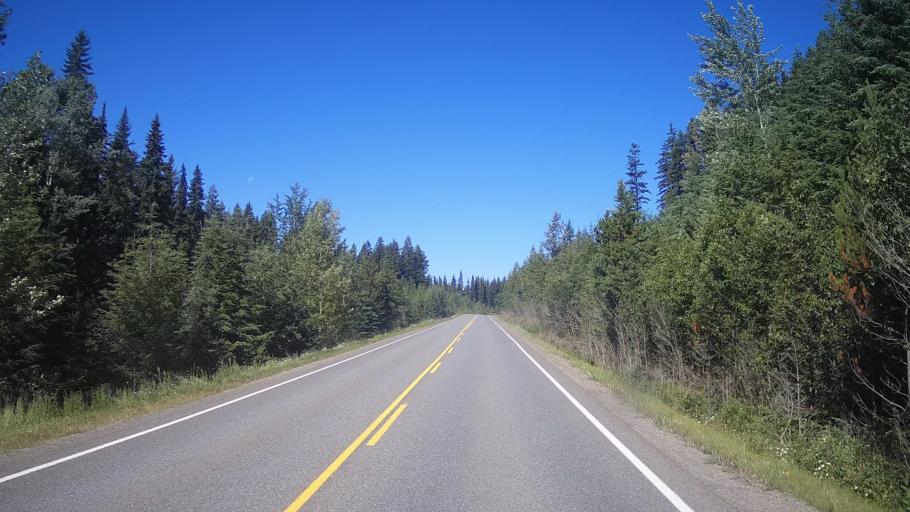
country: CA
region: British Columbia
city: Kamloops
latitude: 51.4970
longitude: -120.4244
